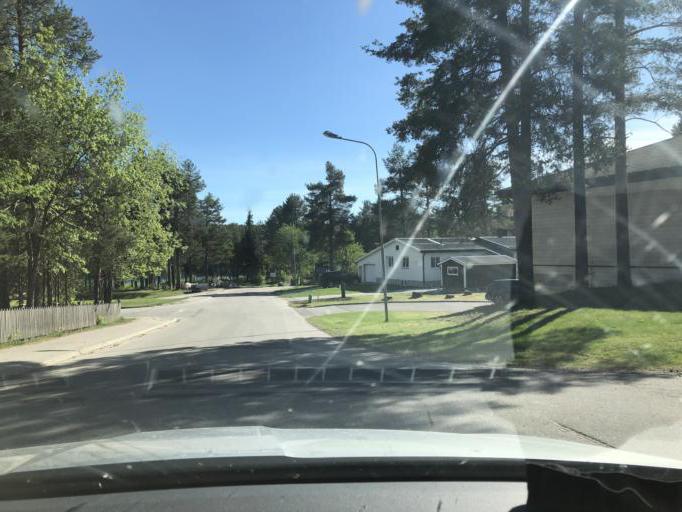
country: SE
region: Norrbotten
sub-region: Jokkmokks Kommun
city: Jokkmokk
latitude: 66.6033
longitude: 19.8291
